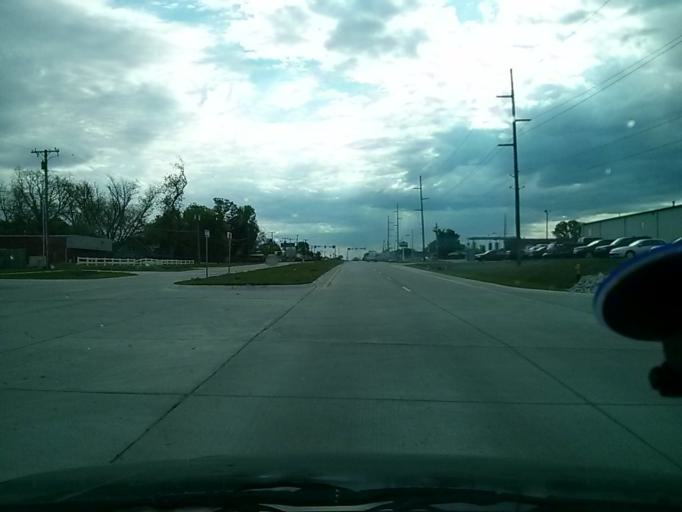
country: US
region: Oklahoma
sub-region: Tulsa County
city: Owasso
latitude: 36.1606
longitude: -95.8546
